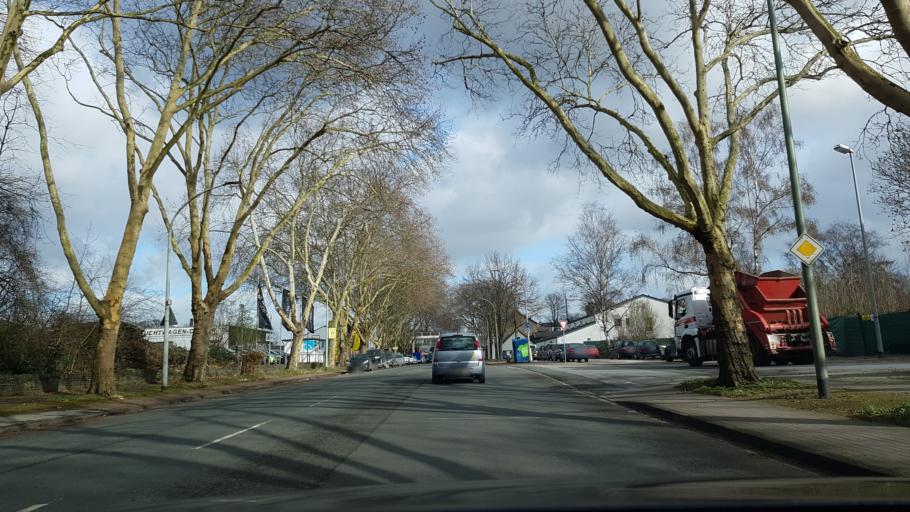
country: DE
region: North Rhine-Westphalia
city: Meiderich
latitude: 51.4669
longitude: 6.7921
